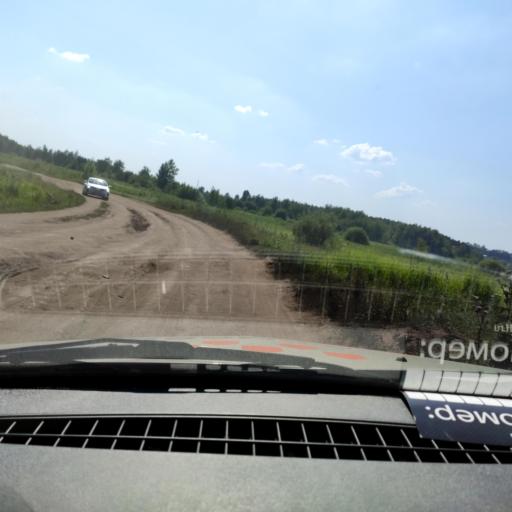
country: RU
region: Bashkortostan
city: Avdon
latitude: 54.6545
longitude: 55.8036
